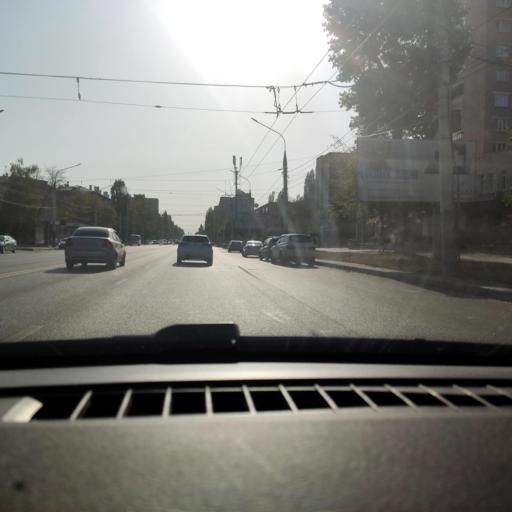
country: RU
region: Voronezj
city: Voronezh
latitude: 51.6536
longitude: 39.2429
